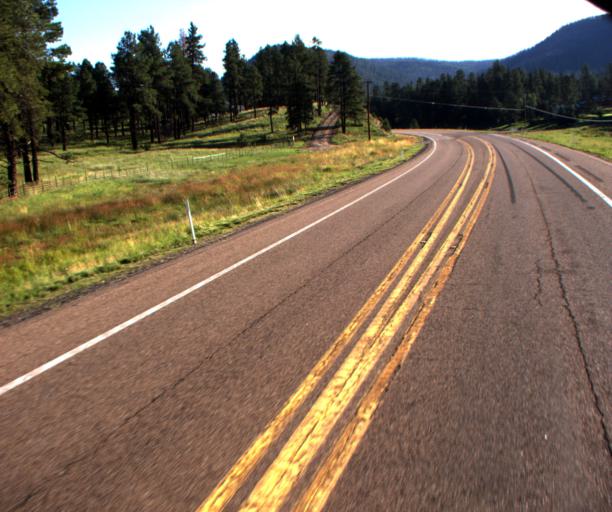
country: US
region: Arizona
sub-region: Apache County
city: Eagar
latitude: 33.8822
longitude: -109.1608
